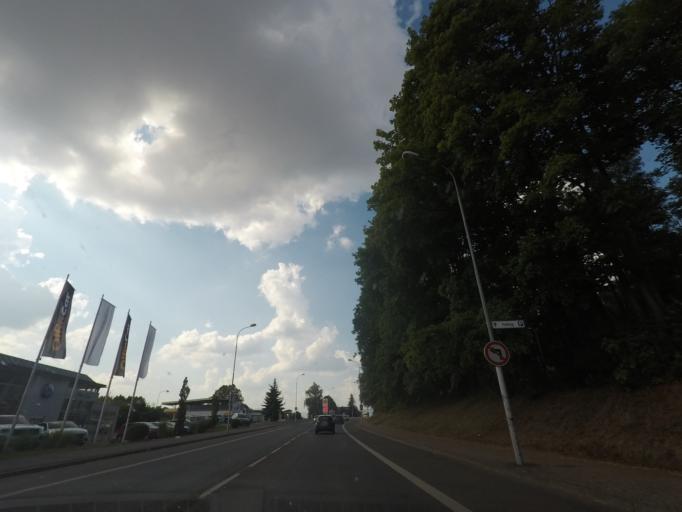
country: CZ
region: Kralovehradecky
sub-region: Okres Trutnov
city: Trutnov
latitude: 50.5533
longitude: 15.9050
